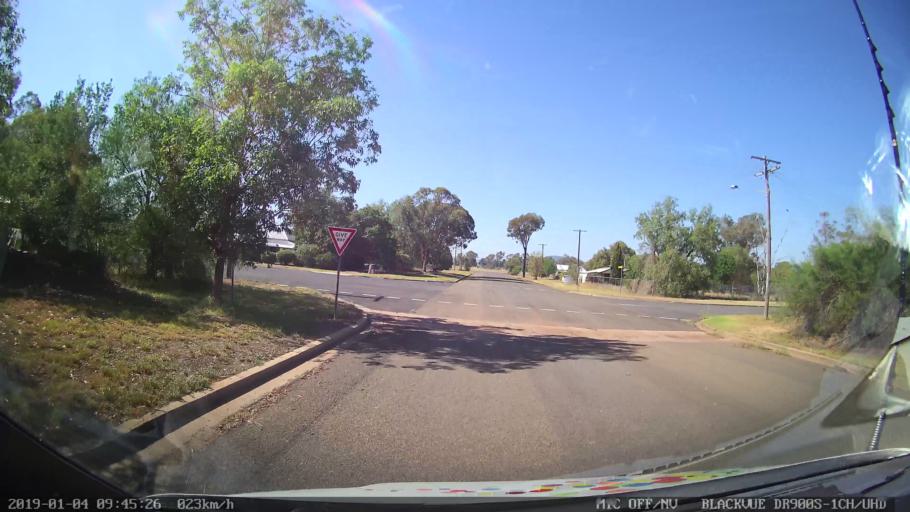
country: AU
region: New South Wales
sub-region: Cabonne
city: Canowindra
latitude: -33.6158
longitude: 148.4329
